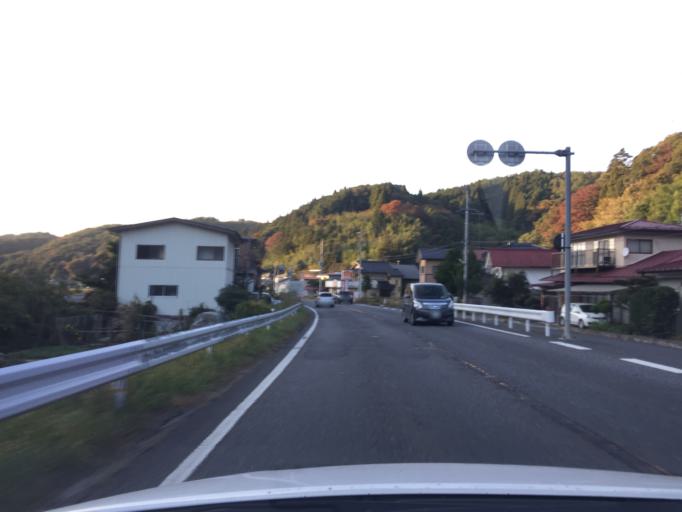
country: JP
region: Fukushima
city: Sukagawa
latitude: 37.3071
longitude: 140.4887
